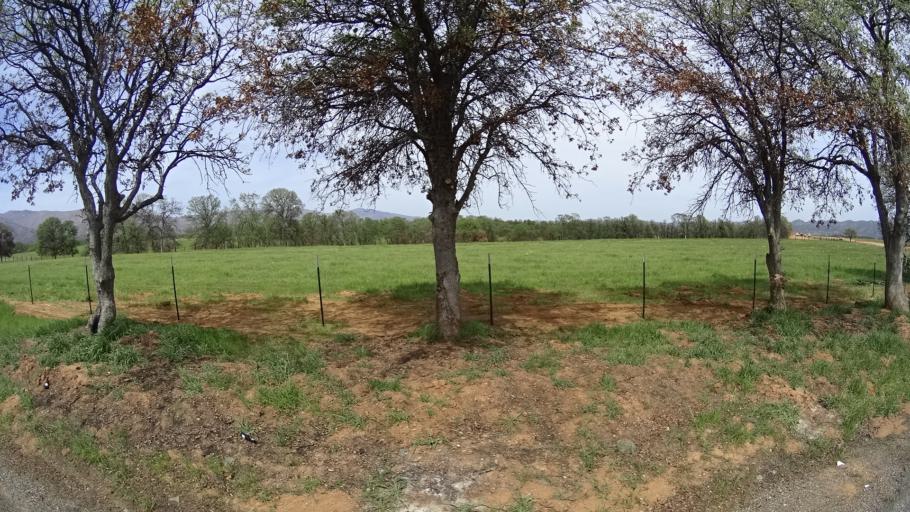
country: US
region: California
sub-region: Glenn County
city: Willows
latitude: 39.5916
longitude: -122.5697
